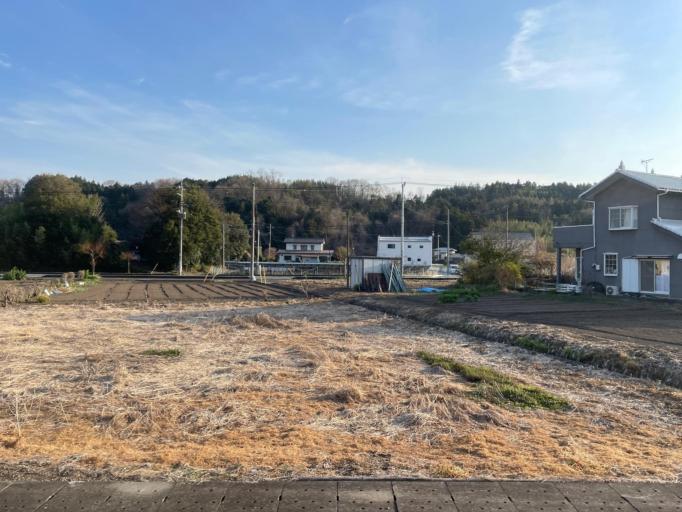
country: JP
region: Gunma
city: Annaka
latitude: 36.2971
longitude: 138.8259
